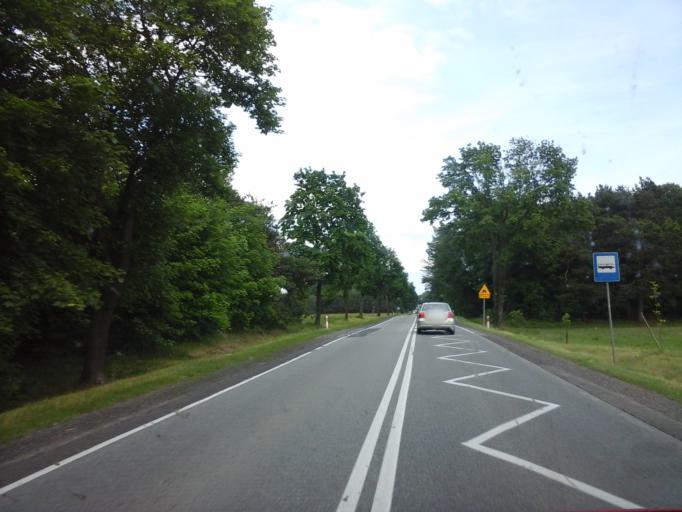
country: PL
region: Lodz Voivodeship
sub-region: Powiat opoczynski
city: Paradyz
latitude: 51.3119
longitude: 20.0834
